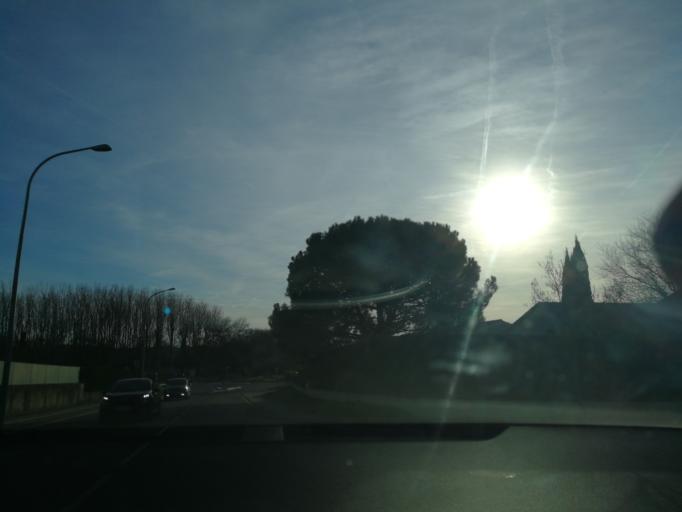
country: FR
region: Midi-Pyrenees
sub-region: Departement de la Haute-Garonne
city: Saint-Jean
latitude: 43.6494
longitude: 1.4963
